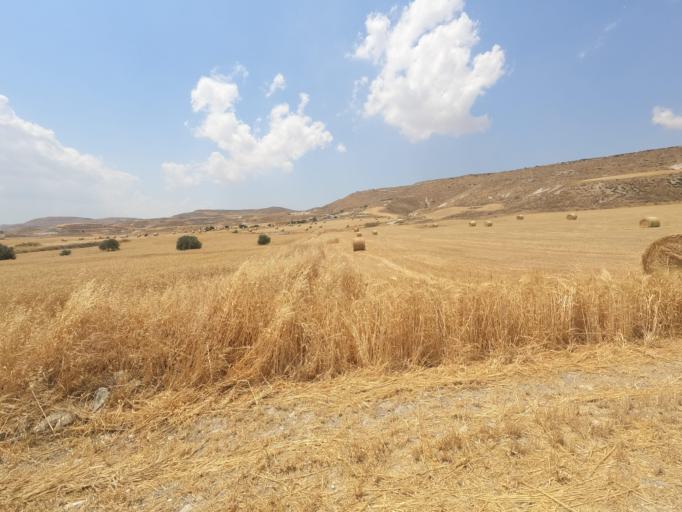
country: CY
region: Larnaka
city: Troulloi
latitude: 35.0366
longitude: 33.5998
